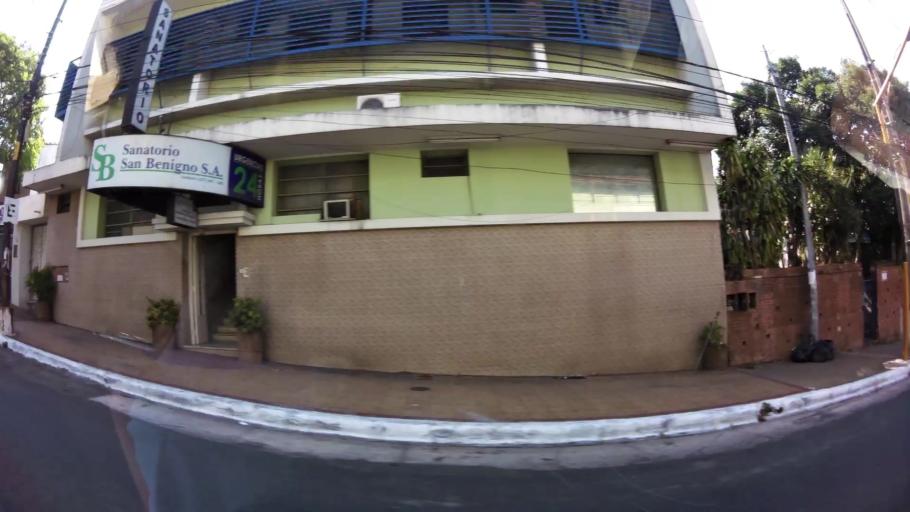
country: PY
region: Asuncion
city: Asuncion
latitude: -25.2944
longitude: -57.6312
